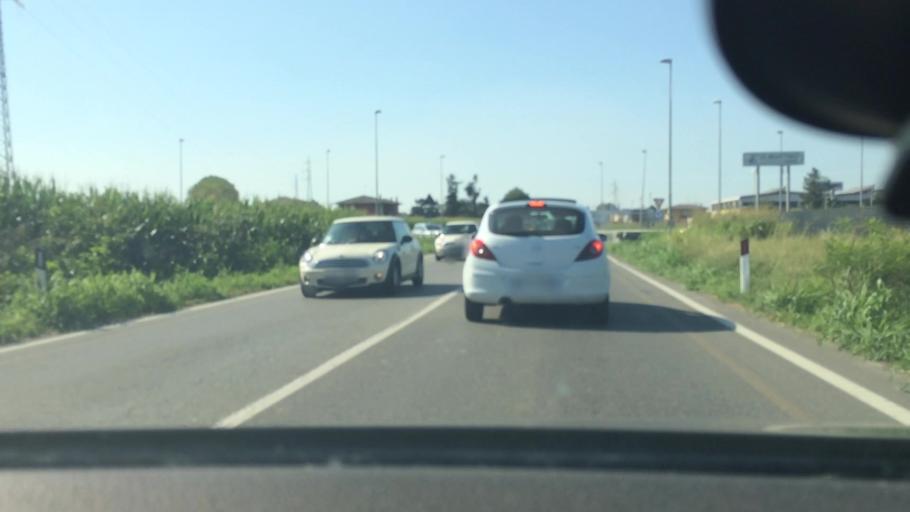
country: IT
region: Lombardy
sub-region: Provincia di Lodi
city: Guardamiglio
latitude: 45.0968
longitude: 9.6881
